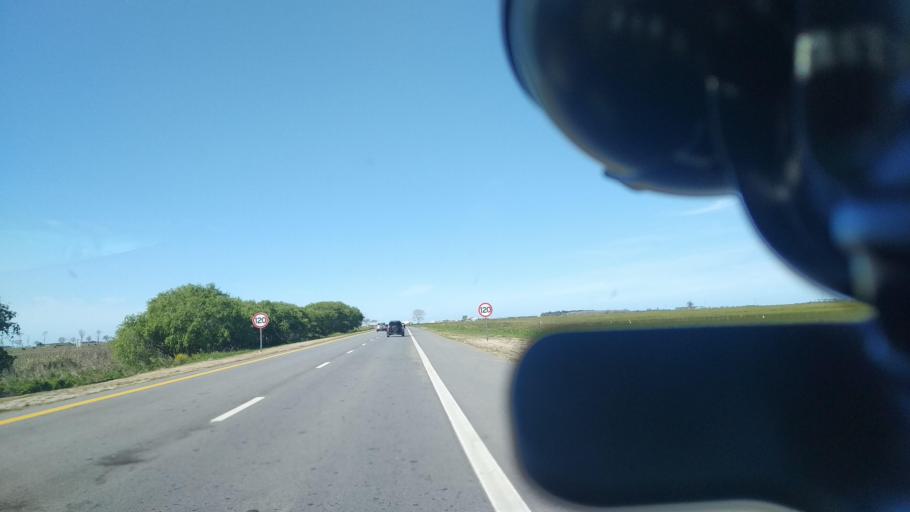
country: AR
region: Buenos Aires
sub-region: Partido de General Lavalle
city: General Lavalle
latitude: -36.4332
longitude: -56.9249
